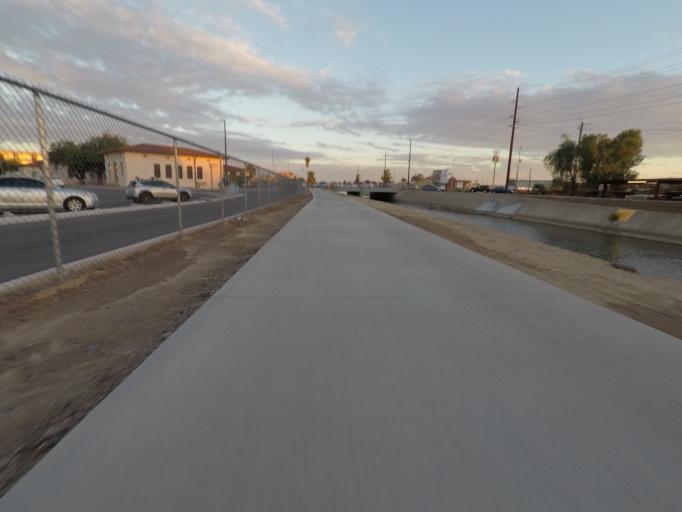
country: US
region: Arizona
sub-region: Maricopa County
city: Phoenix
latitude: 33.4955
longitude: -112.0495
